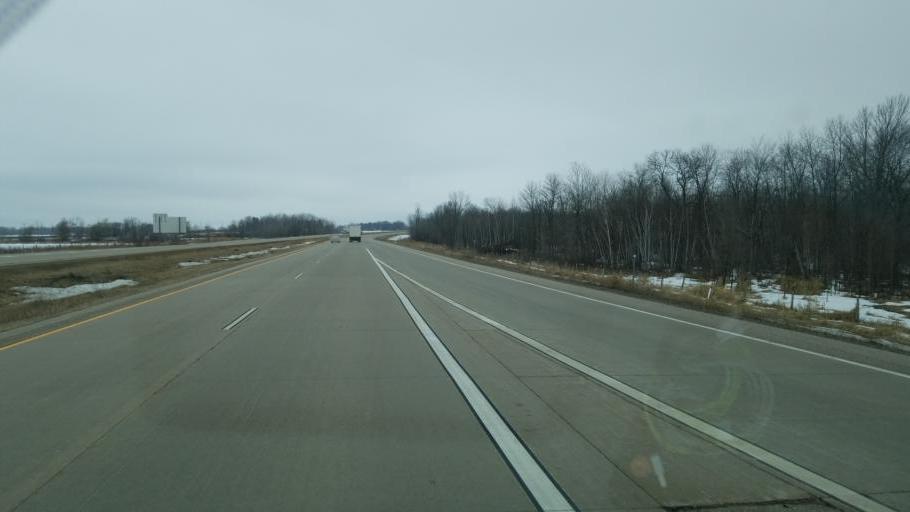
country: US
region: Wisconsin
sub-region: Wood County
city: Wisconsin Rapids
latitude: 44.5995
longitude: -89.8113
